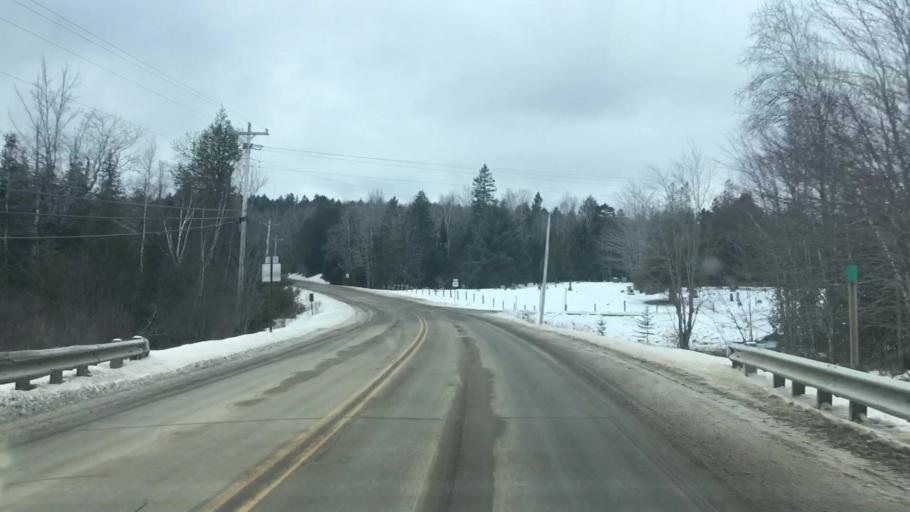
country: US
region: Maine
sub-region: Washington County
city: Calais
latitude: 45.0054
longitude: -67.4162
